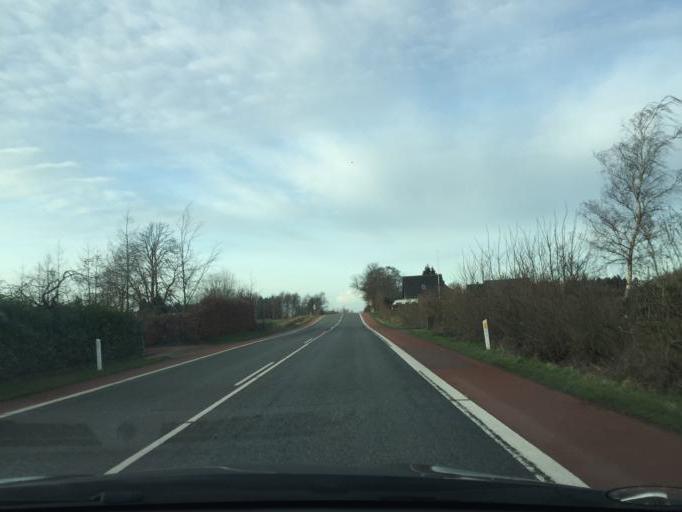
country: DK
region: South Denmark
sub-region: Faaborg-Midtfyn Kommune
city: Ringe
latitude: 55.2667
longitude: 10.4559
